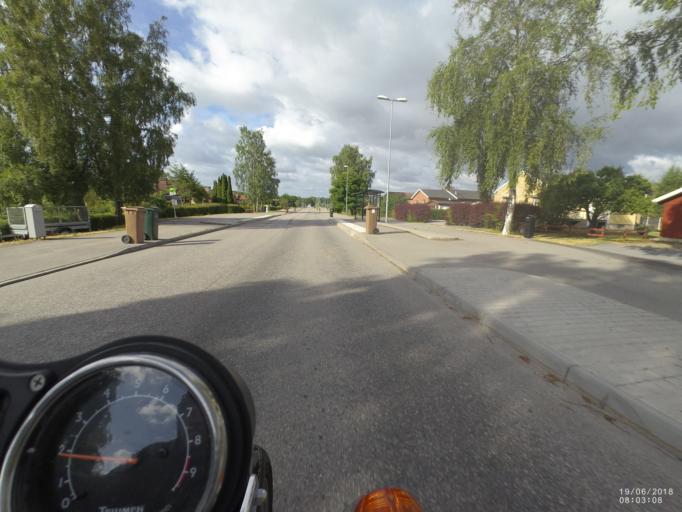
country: SE
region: Soedermanland
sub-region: Nykopings Kommun
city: Nykoping
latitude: 58.7789
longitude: 16.9815
